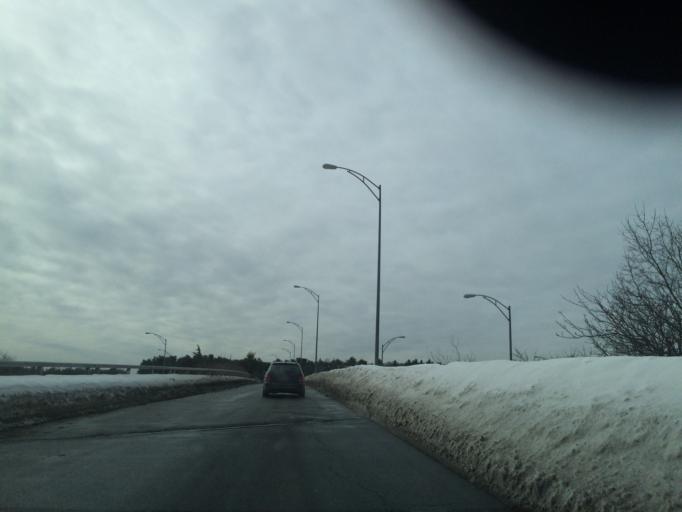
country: US
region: Massachusetts
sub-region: Middlesex County
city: Weston
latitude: 42.3415
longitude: -71.2657
